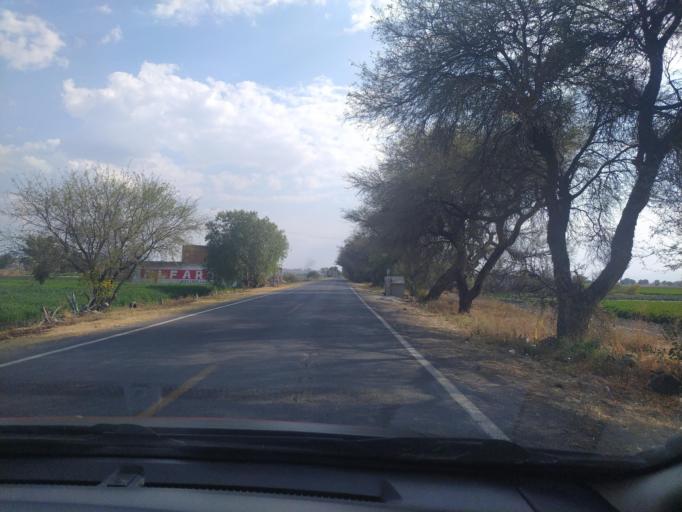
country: MX
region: Guanajuato
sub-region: San Francisco del Rincon
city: San Ignacio de Hidalgo
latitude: 20.9063
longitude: -101.8576
